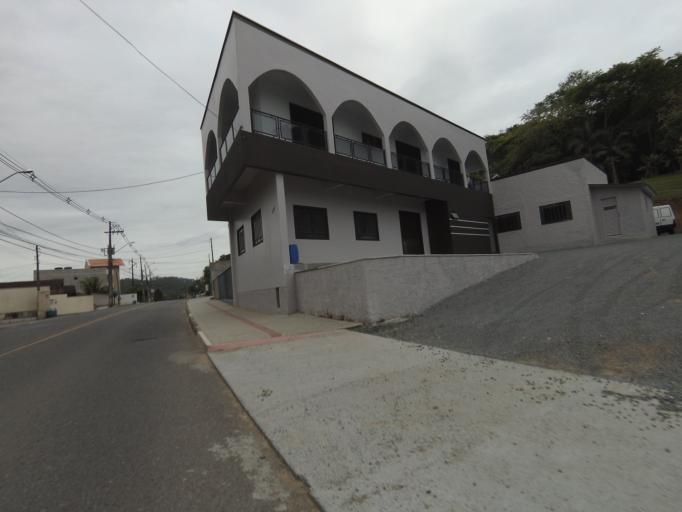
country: BR
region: Santa Catarina
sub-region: Blumenau
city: Blumenau
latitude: -26.8979
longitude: -49.1278
